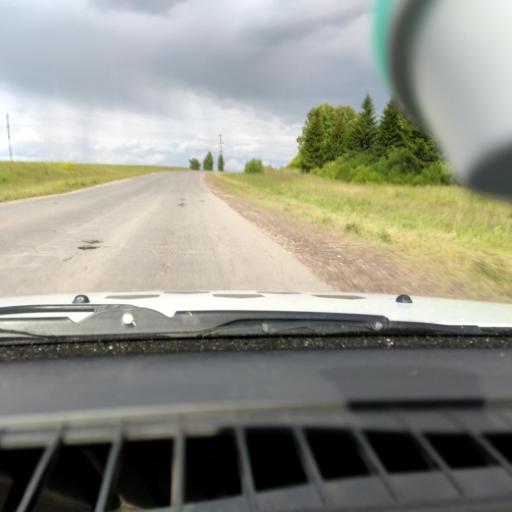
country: RU
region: Perm
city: Orda
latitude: 57.1900
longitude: 56.8586
